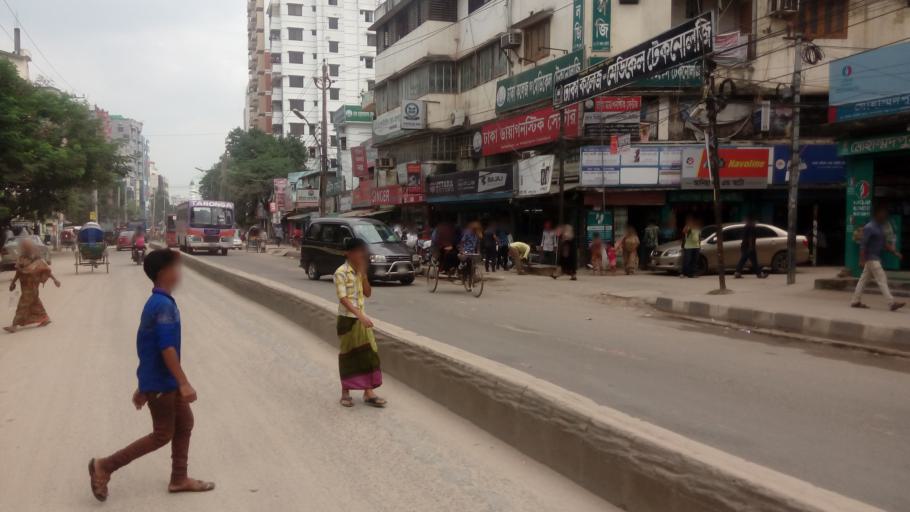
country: BD
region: Dhaka
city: Azimpur
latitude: 23.7573
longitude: 90.3620
